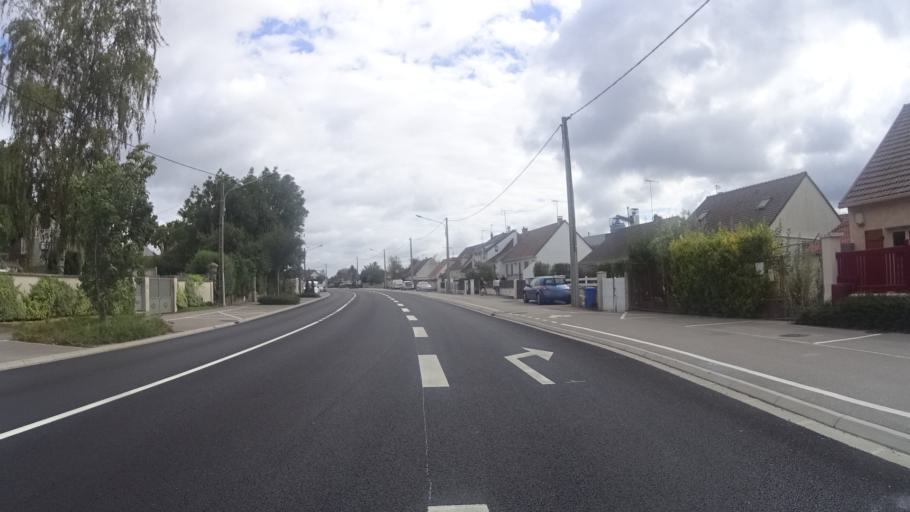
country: FR
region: Picardie
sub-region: Departement de l'Oise
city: Clairoix
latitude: 49.4412
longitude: 2.8593
